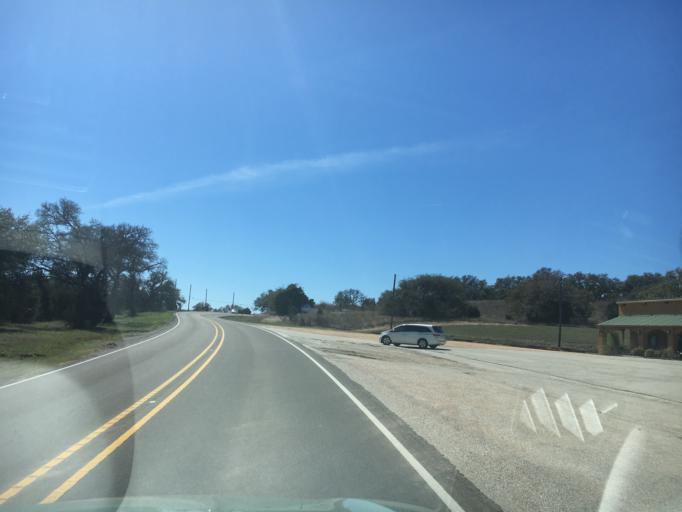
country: US
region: Texas
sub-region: Travis County
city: The Hills
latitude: 30.2981
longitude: -98.0069
